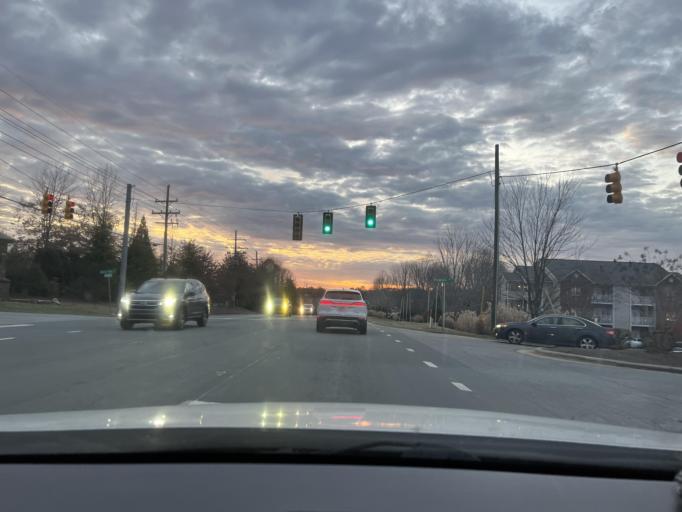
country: US
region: North Carolina
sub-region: Guilford County
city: Gibsonville
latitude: 36.0672
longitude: -79.5925
